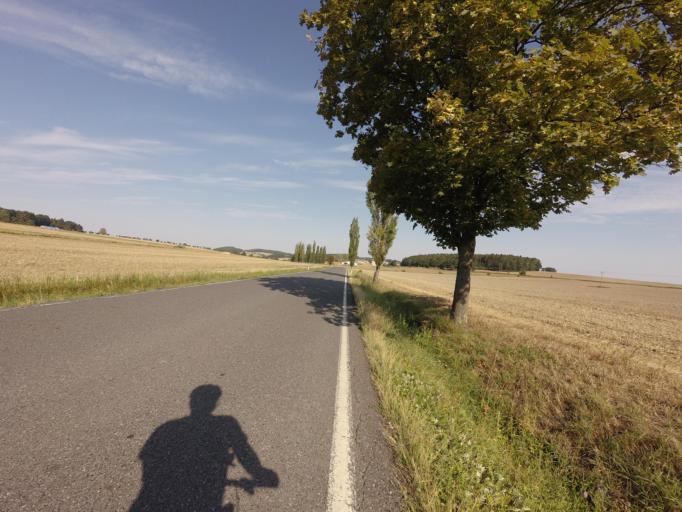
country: CZ
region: Jihocesky
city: Bernartice
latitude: 49.3208
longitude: 14.3664
